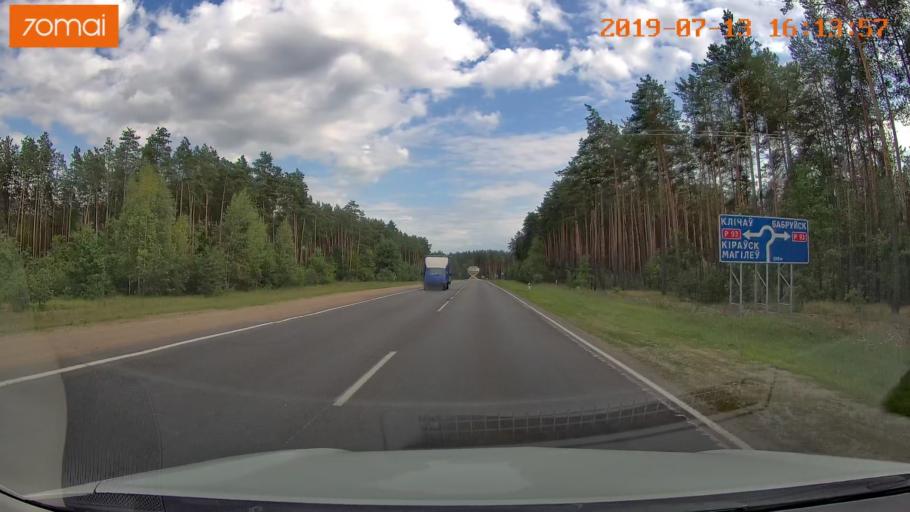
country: BY
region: Mogilev
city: Babruysk
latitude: 53.1592
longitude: 29.3135
